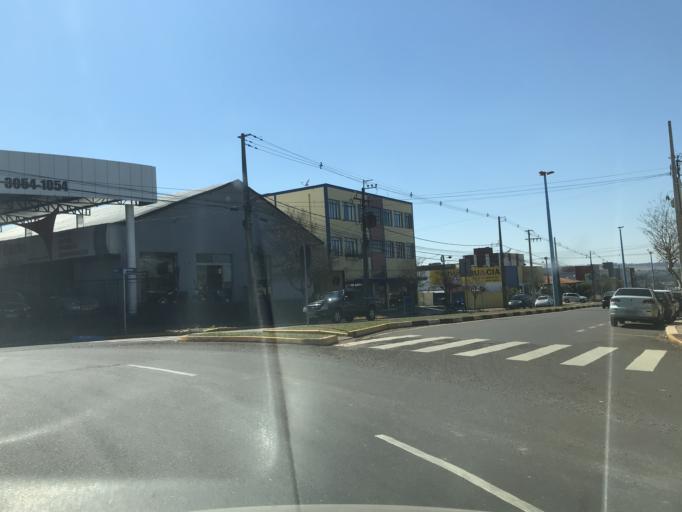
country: BR
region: Parana
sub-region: Toledo
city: Toledo
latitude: -24.7344
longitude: -53.7360
